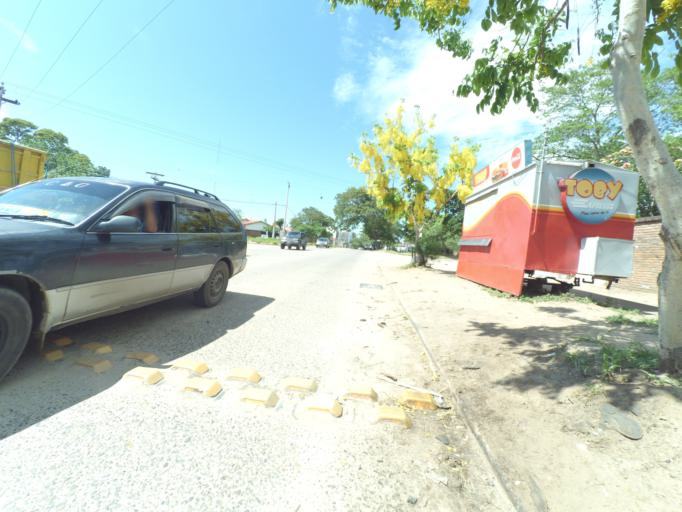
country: BO
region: Santa Cruz
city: Santa Cruz de la Sierra
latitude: -17.8074
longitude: -63.2279
